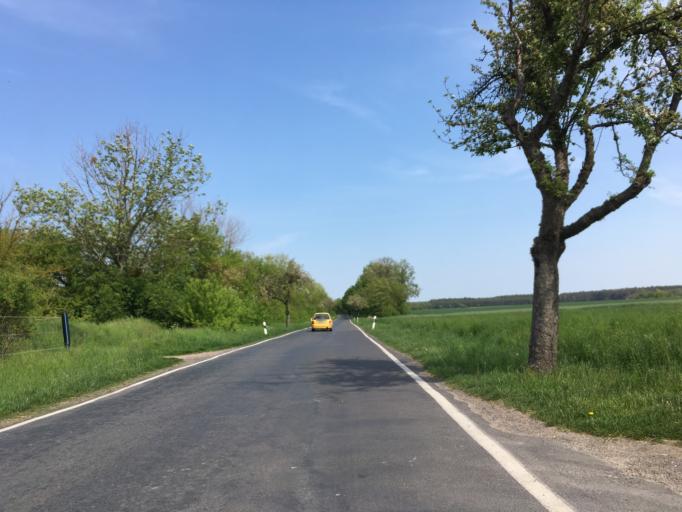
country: DE
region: Brandenburg
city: Werneuchen
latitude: 52.6540
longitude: 13.7296
